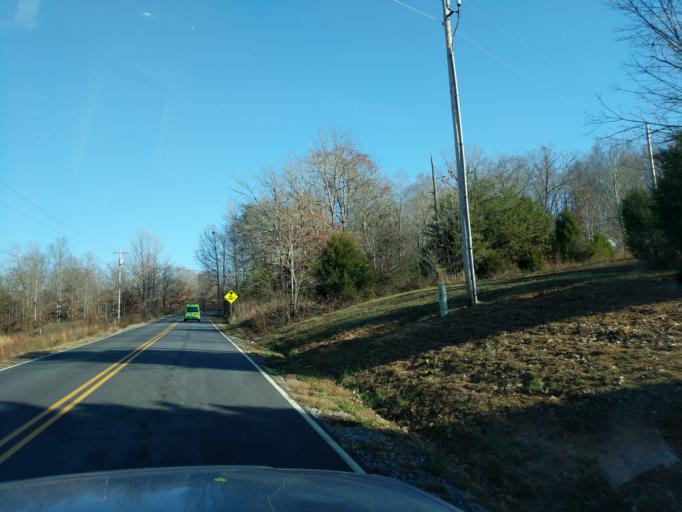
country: US
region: North Carolina
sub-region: Rutherford County
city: Rutherfordton
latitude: 35.2688
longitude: -82.0398
